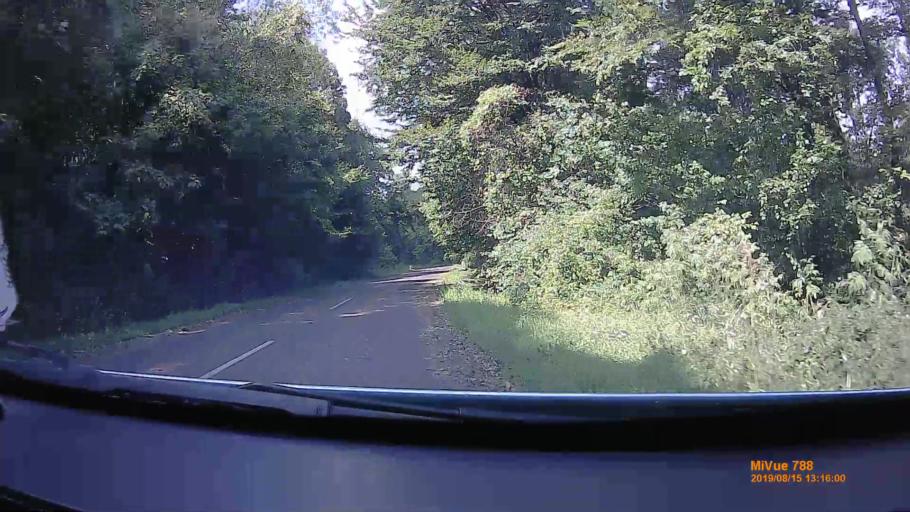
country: HU
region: Borsod-Abauj-Zemplen
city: Sajobabony
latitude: 48.1567
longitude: 20.6655
